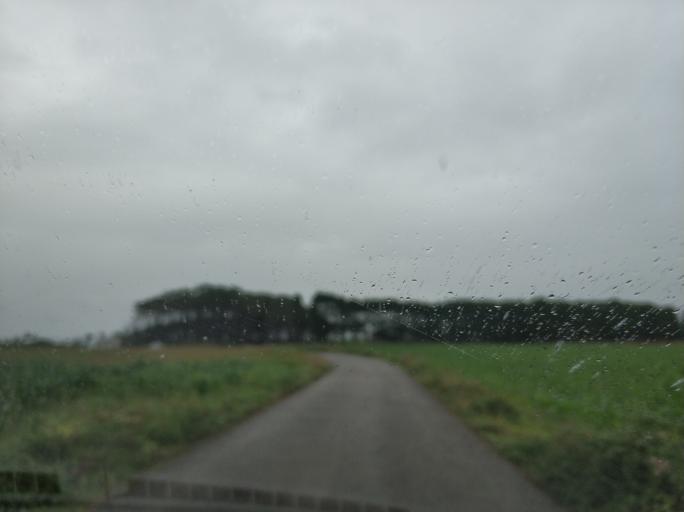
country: ES
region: Asturias
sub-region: Province of Asturias
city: Tineo
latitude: 43.5637
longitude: -6.4698
